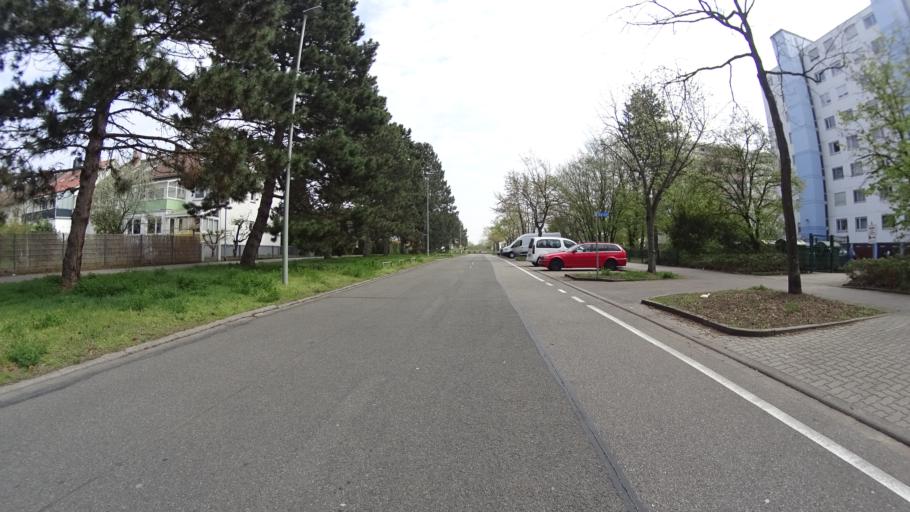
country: DE
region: Baden-Wuerttemberg
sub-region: Karlsruhe Region
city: Karlsruhe
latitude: 49.0304
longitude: 8.3730
